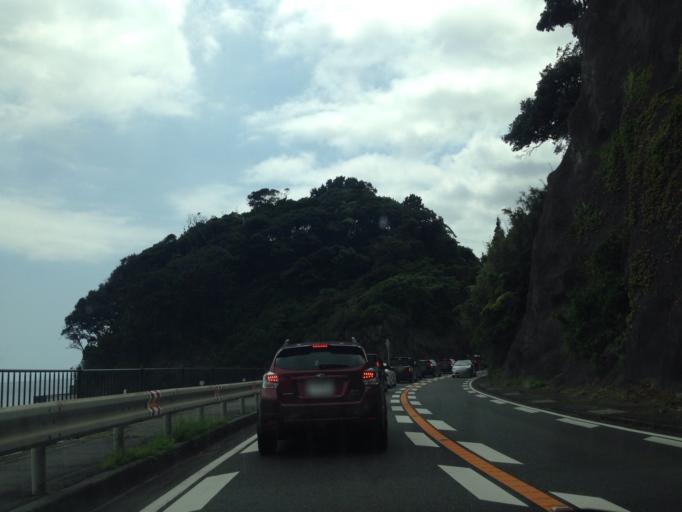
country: JP
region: Shizuoka
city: Shimoda
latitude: 34.7085
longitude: 138.9790
